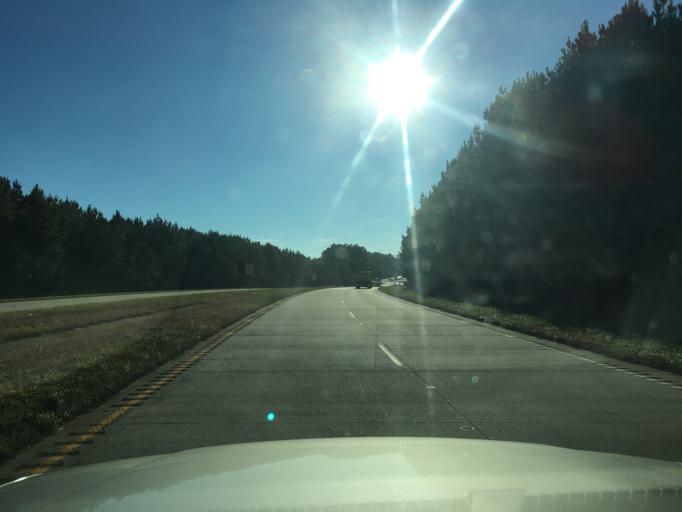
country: US
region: South Carolina
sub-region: Greenville County
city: Greer
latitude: 34.9155
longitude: -82.2063
